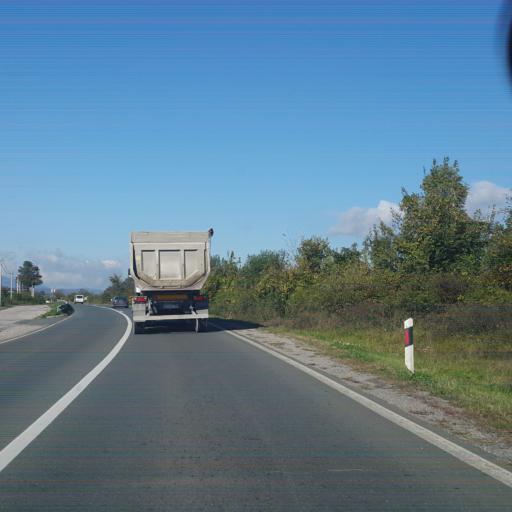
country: RS
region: Central Serbia
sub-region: Rasinski Okrug
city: Trstenik
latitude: 43.6325
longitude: 20.9607
